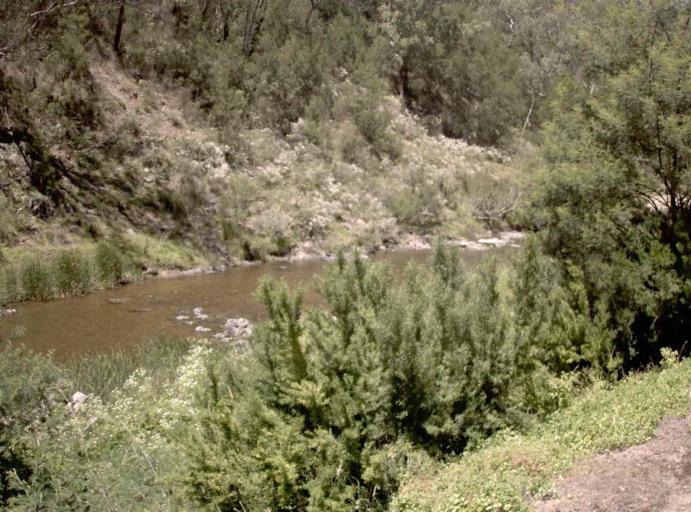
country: AU
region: Victoria
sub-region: East Gippsland
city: Bairnsdale
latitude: -37.4399
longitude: 147.8330
